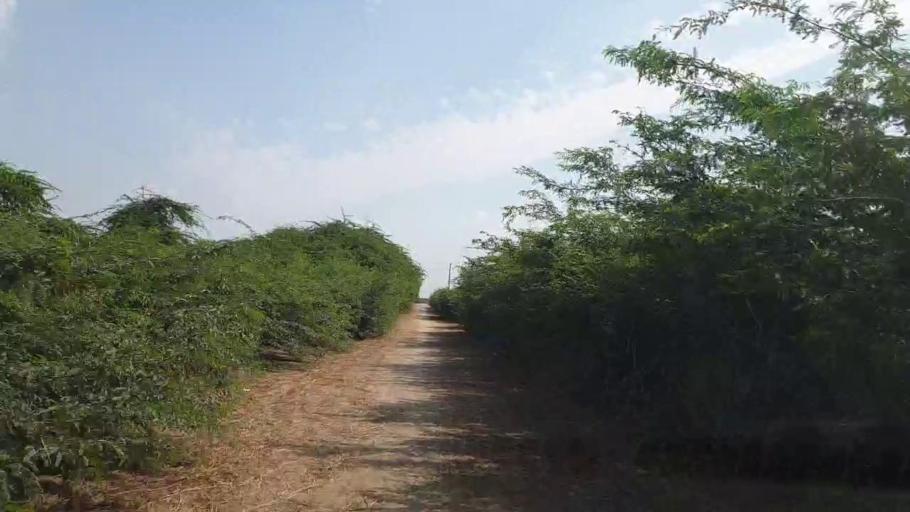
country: PK
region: Sindh
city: Badin
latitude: 24.4786
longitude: 68.6147
